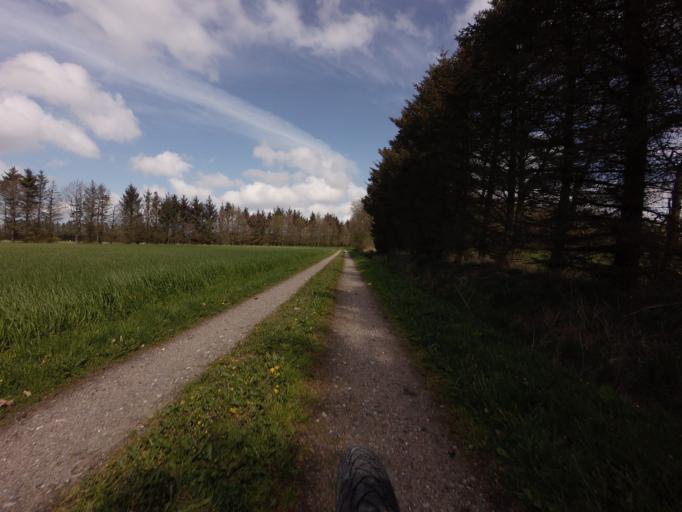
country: DK
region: North Denmark
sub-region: Jammerbugt Kommune
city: Kas
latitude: 57.1961
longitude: 9.5934
